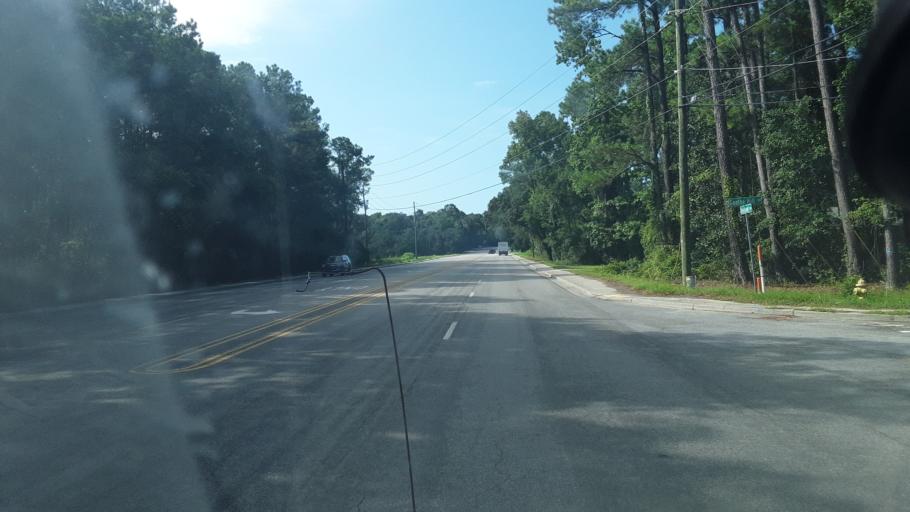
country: US
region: South Carolina
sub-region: Beaufort County
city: Burton
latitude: 32.4189
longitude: -80.7306
